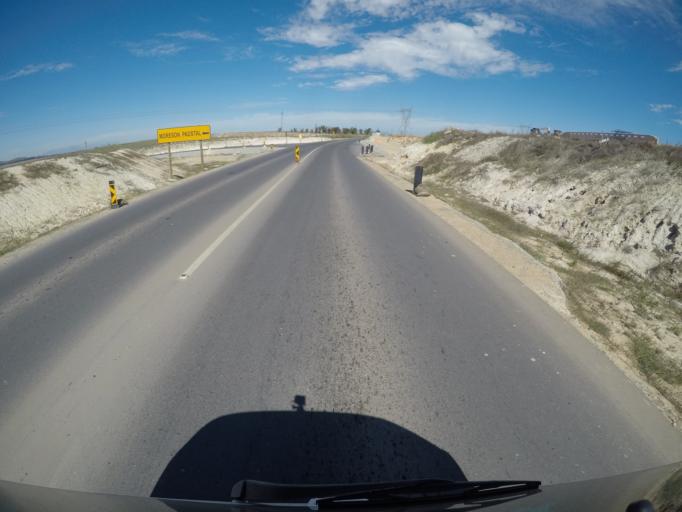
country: ZA
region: Western Cape
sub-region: West Coast District Municipality
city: Malmesbury
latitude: -33.5118
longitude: 18.6577
